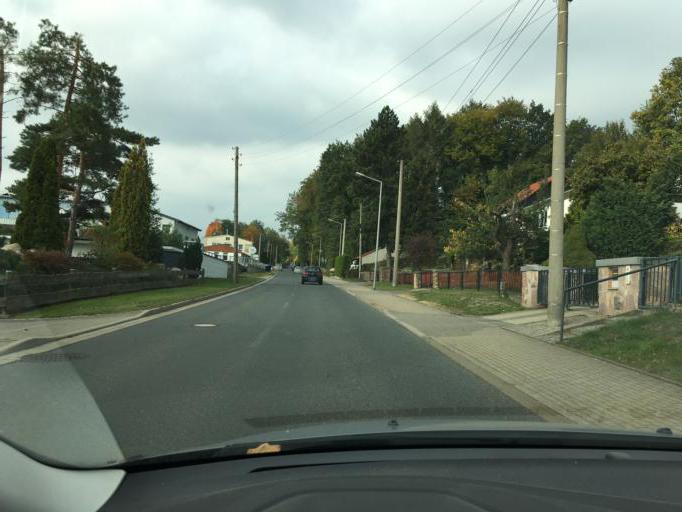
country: DE
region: Saxony
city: Bannewitz
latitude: 50.9904
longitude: 13.7031
